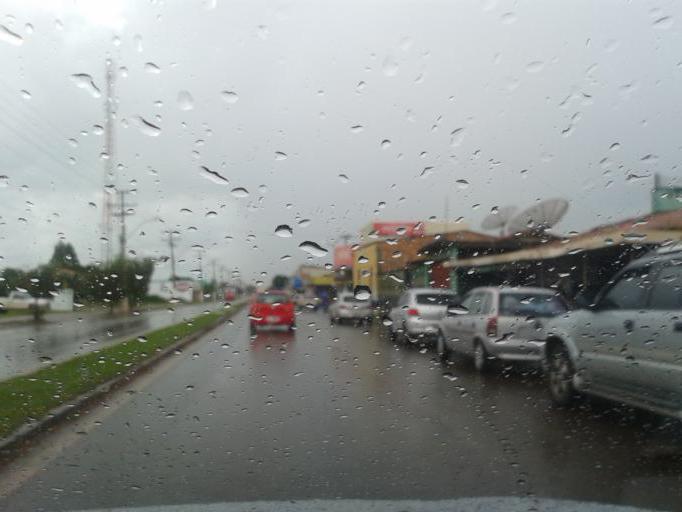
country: BR
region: Goias
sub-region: Itaberai
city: Itaberai
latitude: -16.0371
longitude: -49.7937
